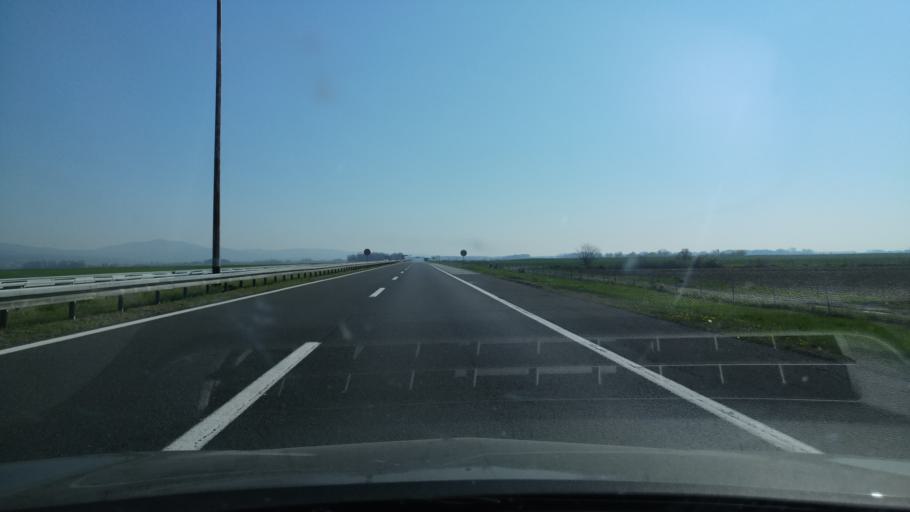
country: HR
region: Brodsko-Posavska
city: Ljupina
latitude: 45.2277
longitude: 17.4160
